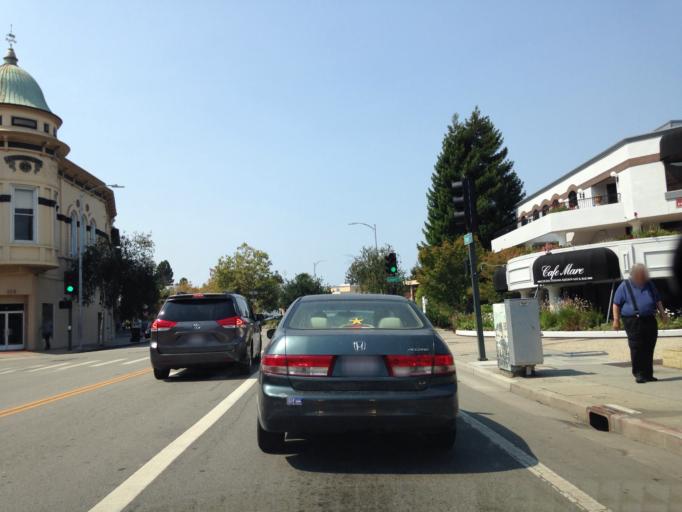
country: US
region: California
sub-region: Santa Cruz County
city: Santa Cruz
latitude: 36.9749
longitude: -122.0253
